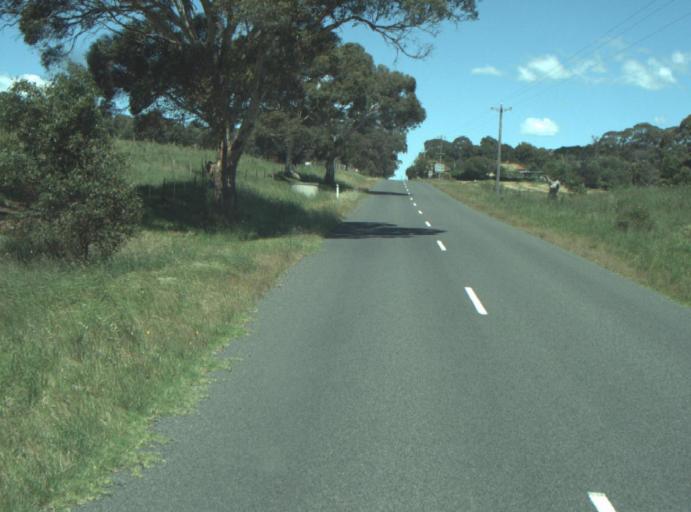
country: AU
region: Victoria
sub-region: Greater Geelong
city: Lara
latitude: -37.8775
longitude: 144.2673
